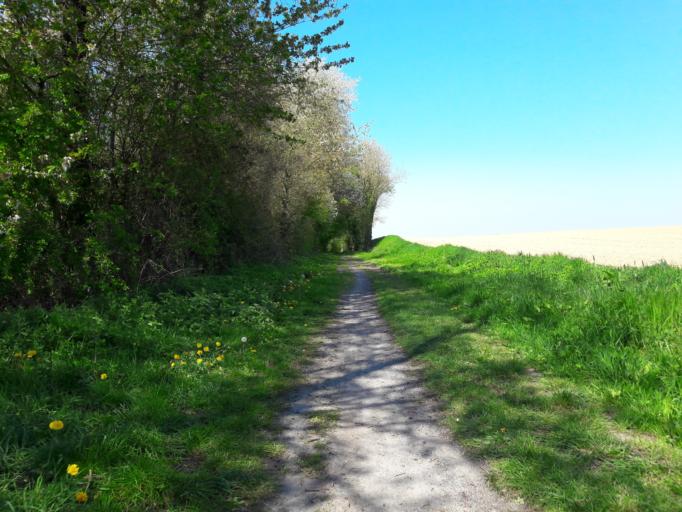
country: FR
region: Nord-Pas-de-Calais
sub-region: Departement du Nord
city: Sains-du-Nord
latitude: 50.1573
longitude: 4.0703
